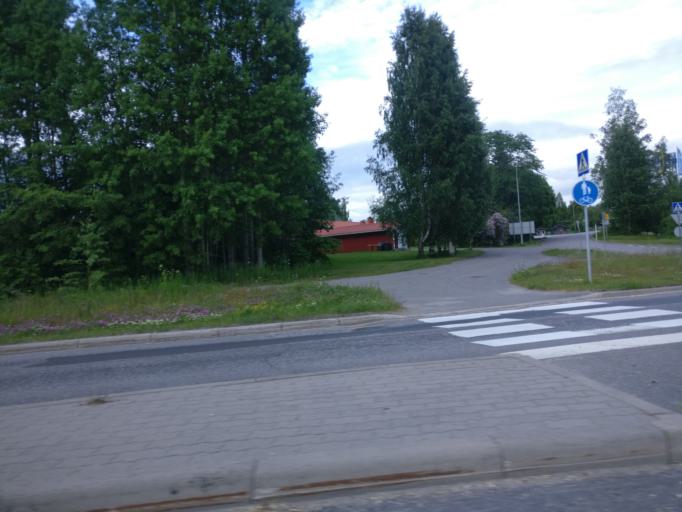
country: FI
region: Southern Savonia
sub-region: Savonlinna
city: Savonlinna
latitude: 61.8767
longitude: 28.9502
